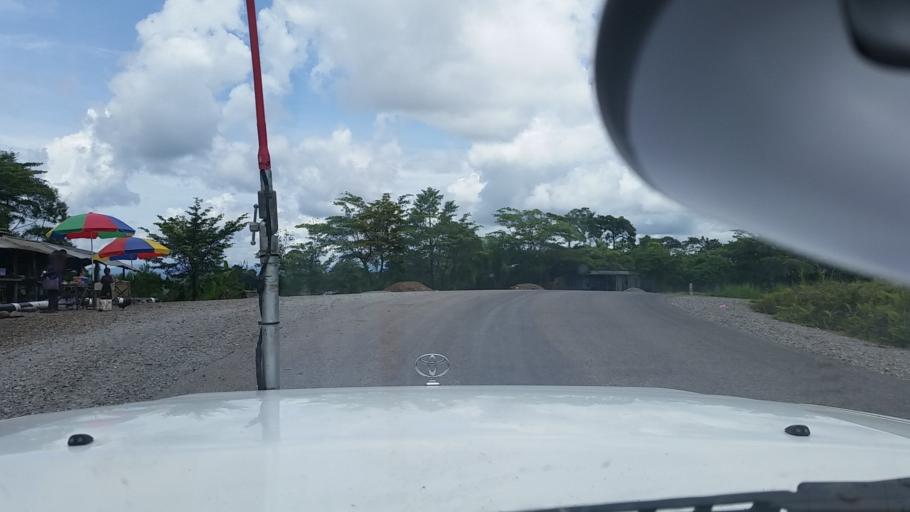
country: PG
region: Western Province
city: Kiunga
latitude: -5.5459
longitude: 141.2725
